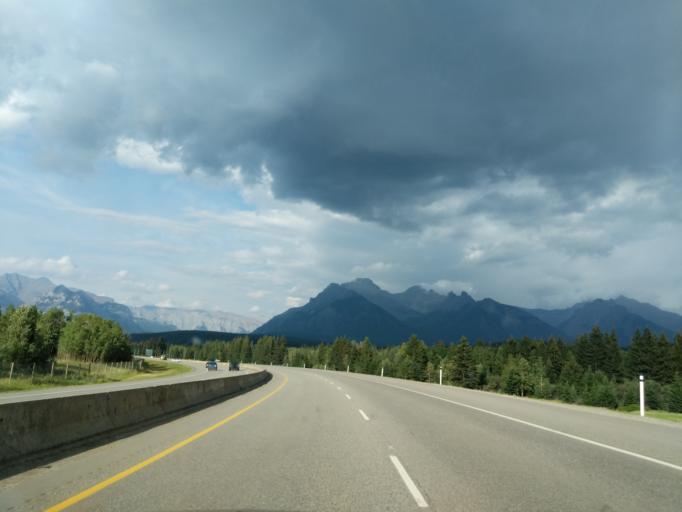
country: CA
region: Alberta
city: Banff
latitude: 51.1964
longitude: -115.5500
